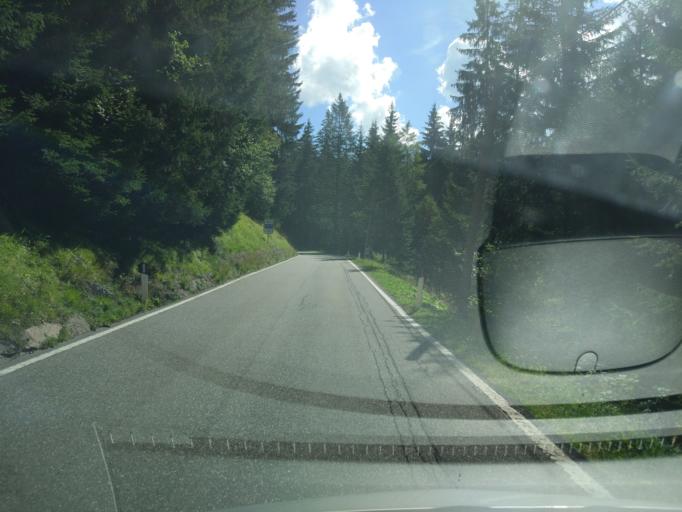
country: IT
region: Trentino-Alto Adige
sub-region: Provincia di Trento
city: Moena
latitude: 46.3077
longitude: 11.6950
